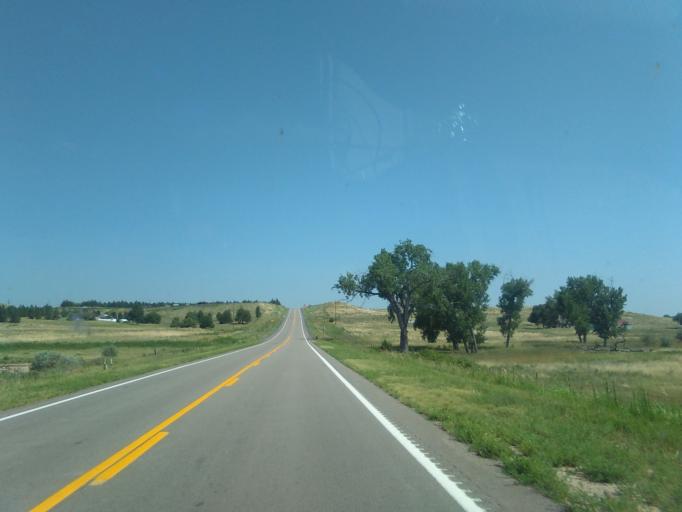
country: US
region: Nebraska
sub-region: Dundy County
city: Benkelman
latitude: 40.0115
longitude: -101.5425
